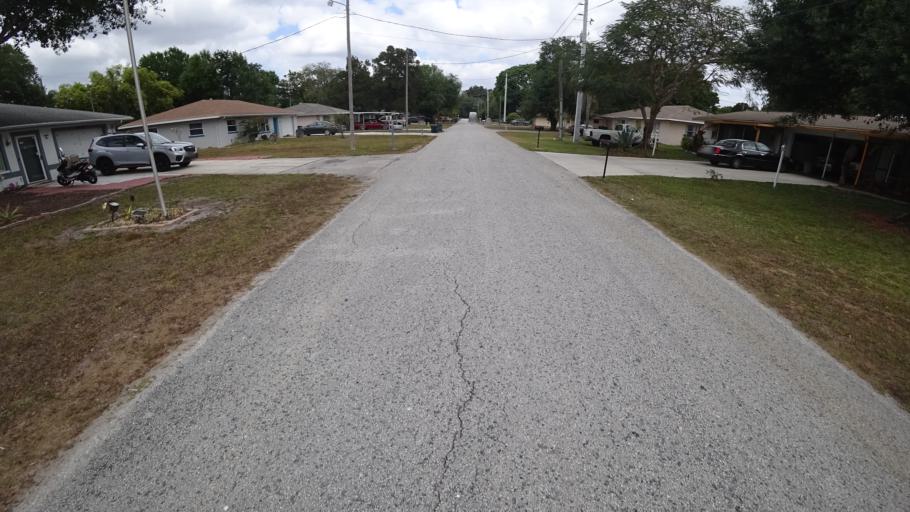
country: US
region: Florida
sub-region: Manatee County
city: South Bradenton
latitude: 27.4449
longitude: -82.5795
